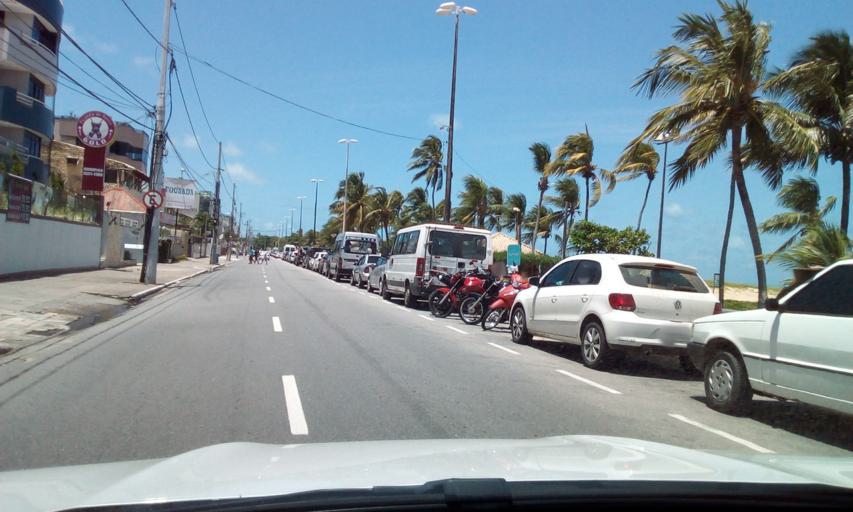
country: BR
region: Paraiba
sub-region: Joao Pessoa
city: Joao Pessoa
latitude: -7.1181
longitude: -34.8235
